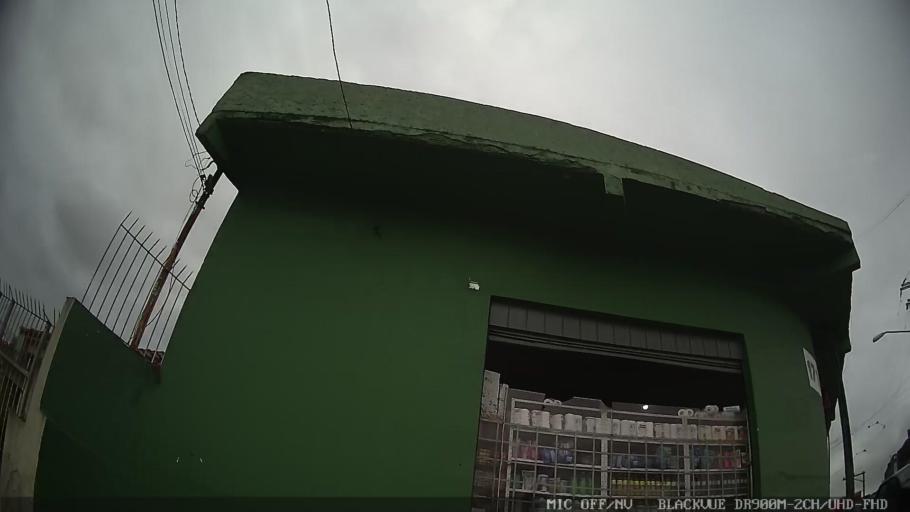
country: BR
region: Sao Paulo
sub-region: Osasco
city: Osasco
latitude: -23.4872
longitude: -46.7442
